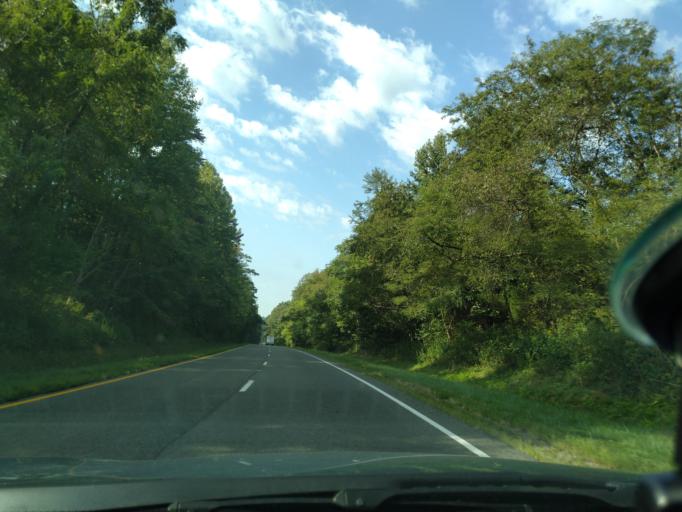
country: US
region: Virginia
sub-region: King George County
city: King George
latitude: 38.1418
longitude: -77.2276
